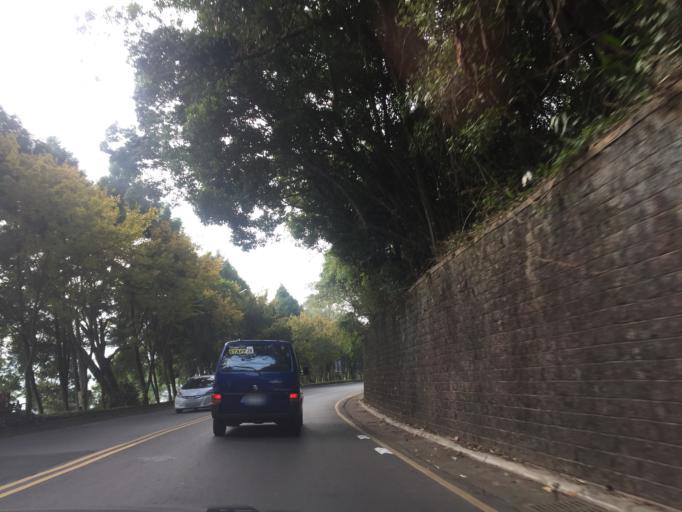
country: TW
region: Taiwan
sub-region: Nantou
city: Puli
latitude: 23.8687
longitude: 120.9162
